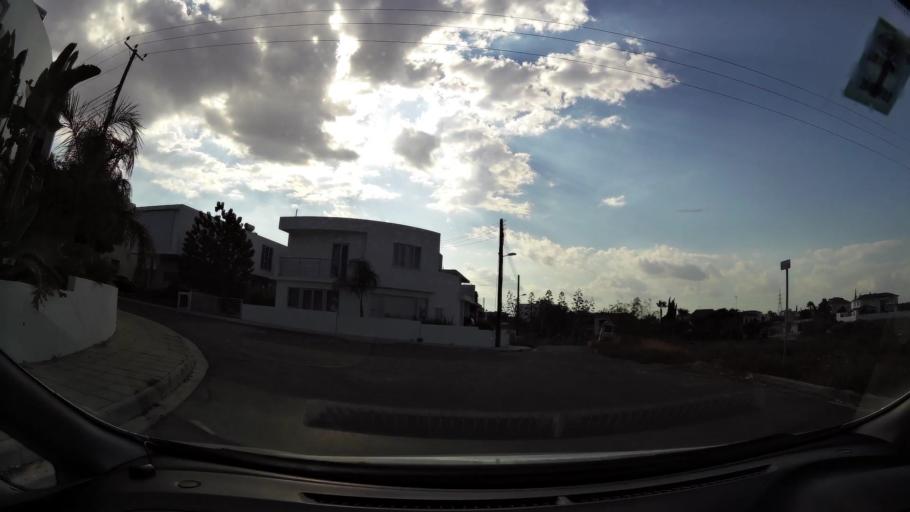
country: CY
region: Larnaka
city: Aradippou
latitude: 34.9428
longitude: 33.6079
